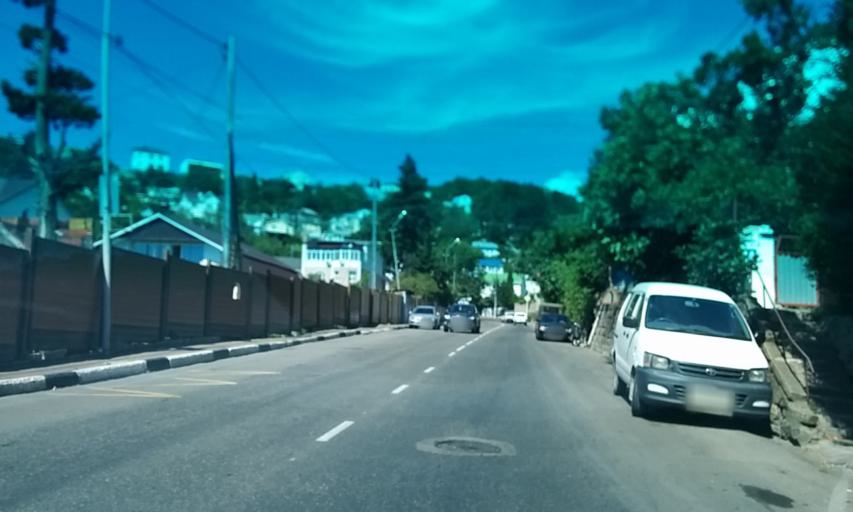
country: RU
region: Krasnodarskiy
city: Tuapse
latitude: 44.1037
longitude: 39.0685
